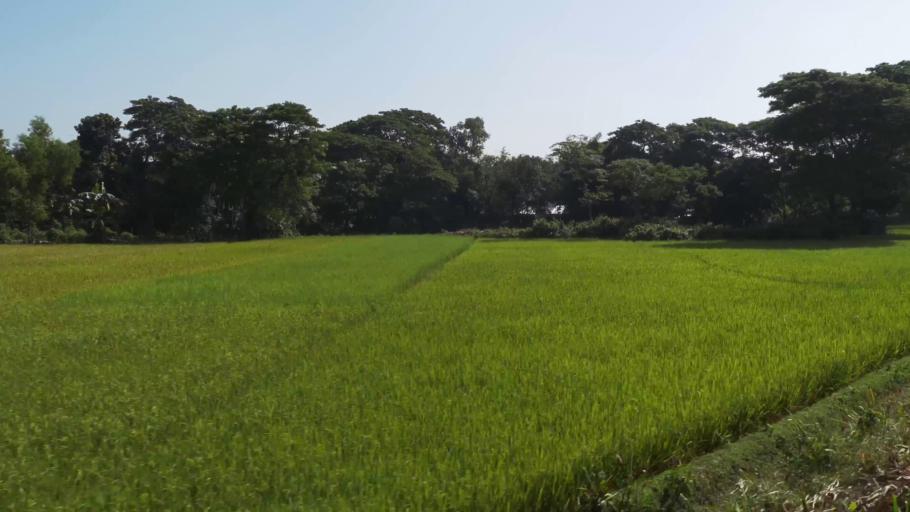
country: BD
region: Dhaka
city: Gafargaon
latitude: 24.5399
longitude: 90.5086
